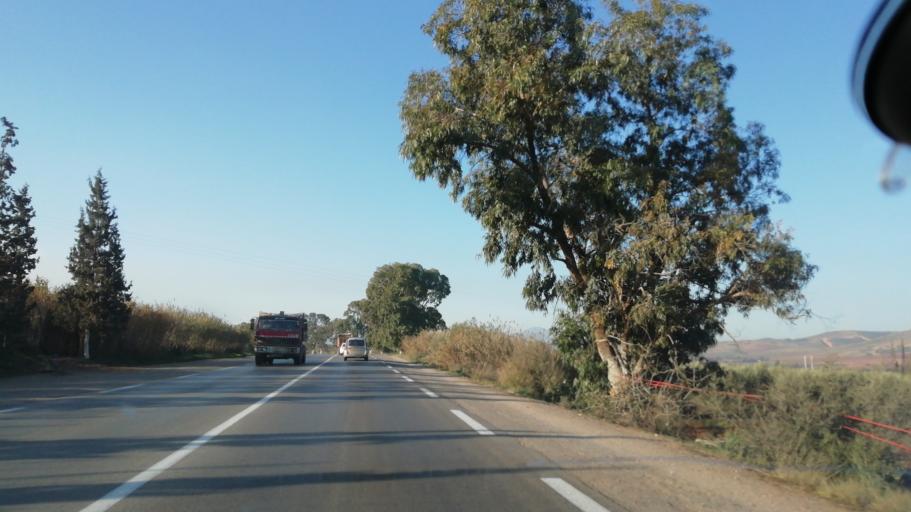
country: DZ
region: Tlemcen
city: Remchi
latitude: 35.0799
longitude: -1.4469
